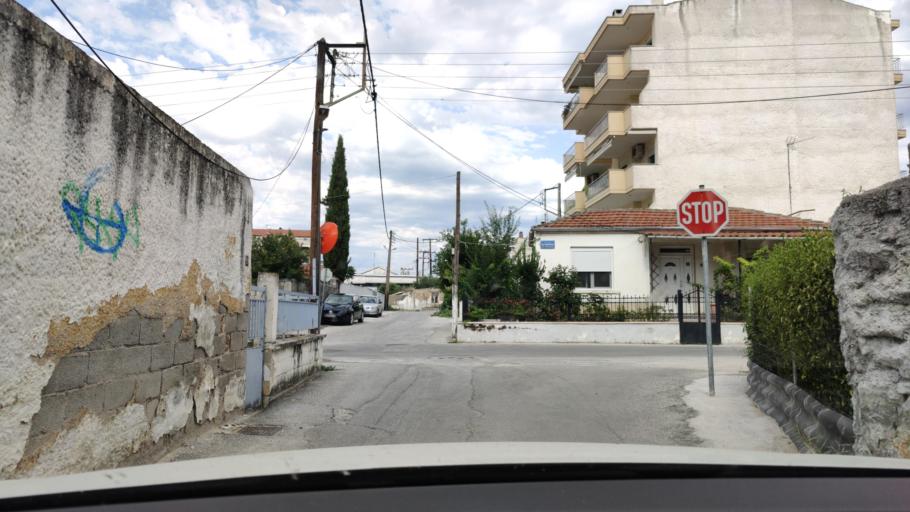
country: GR
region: Central Macedonia
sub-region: Nomos Serron
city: Serres
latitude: 41.0849
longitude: 23.5341
